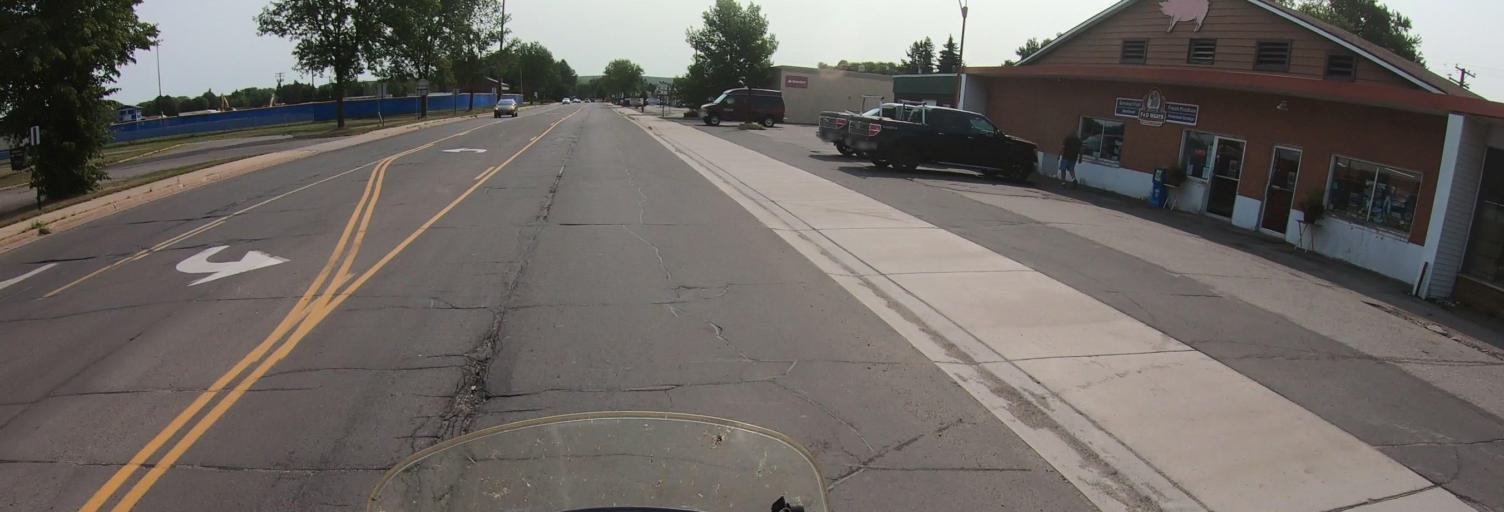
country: US
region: Minnesota
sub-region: Saint Louis County
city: Virginia
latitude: 47.5158
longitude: -92.5511
